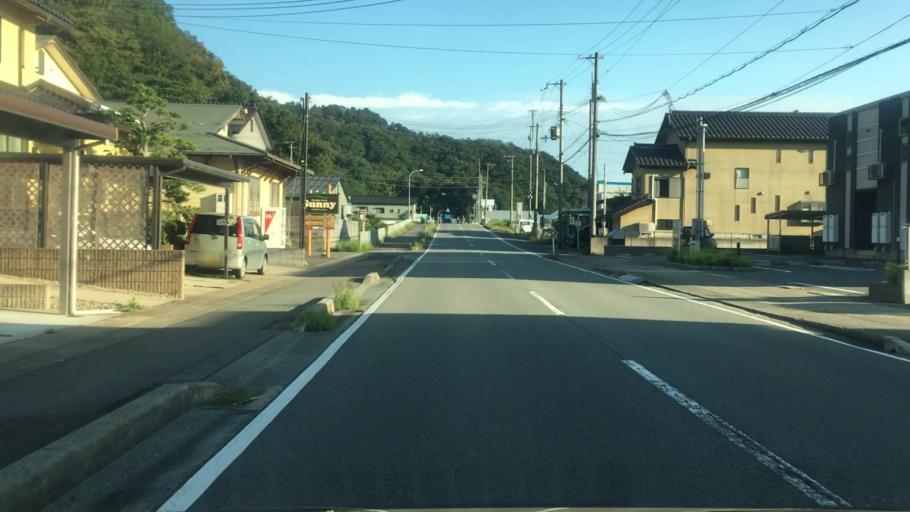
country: JP
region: Hyogo
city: Toyooka
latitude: 35.5617
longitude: 134.8222
